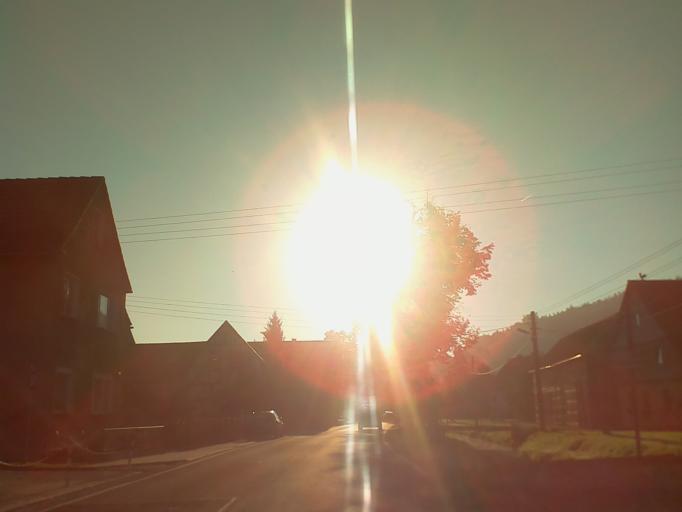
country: DE
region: Thuringia
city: Ottendorf
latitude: 50.8271
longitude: 11.8016
